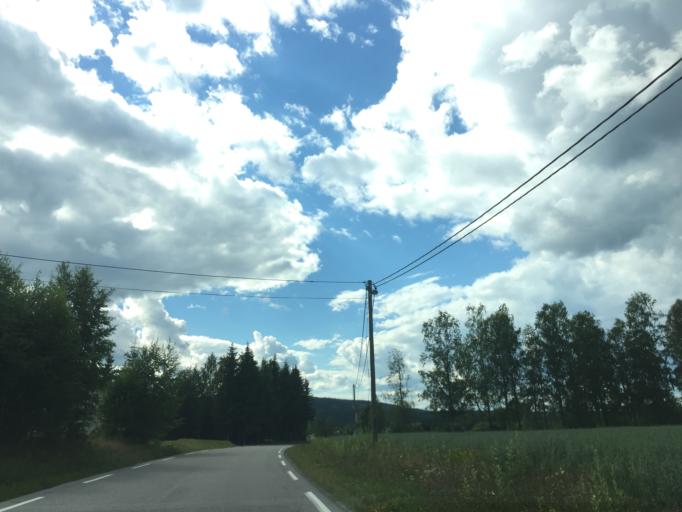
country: NO
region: Hedmark
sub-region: Kongsvinger
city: Spetalen
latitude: 60.1922
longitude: 11.8482
